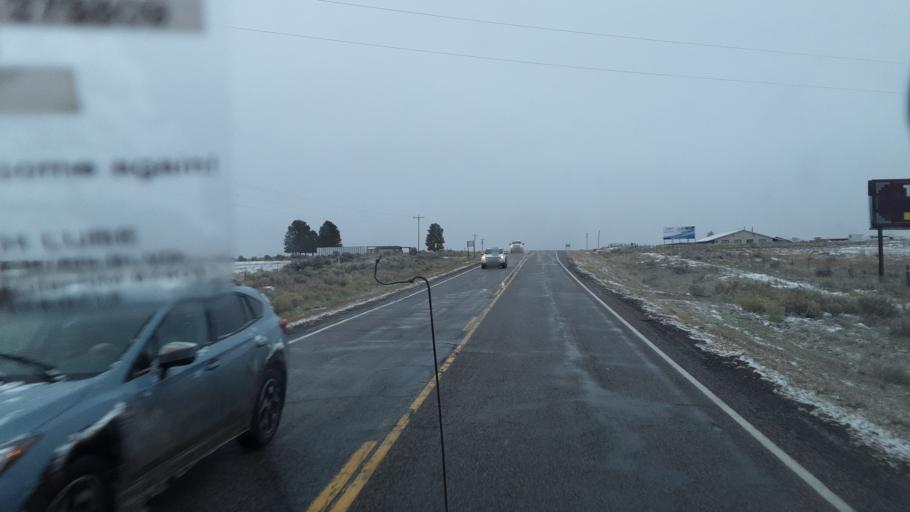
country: US
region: New Mexico
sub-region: Rio Arriba County
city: Tierra Amarilla
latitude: 36.7141
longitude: -106.5605
